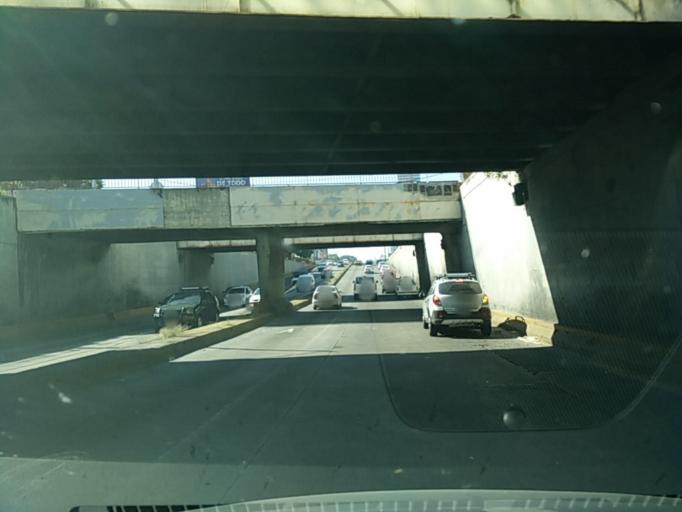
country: MX
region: Jalisco
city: Guadalajara
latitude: 20.6711
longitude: -103.3896
